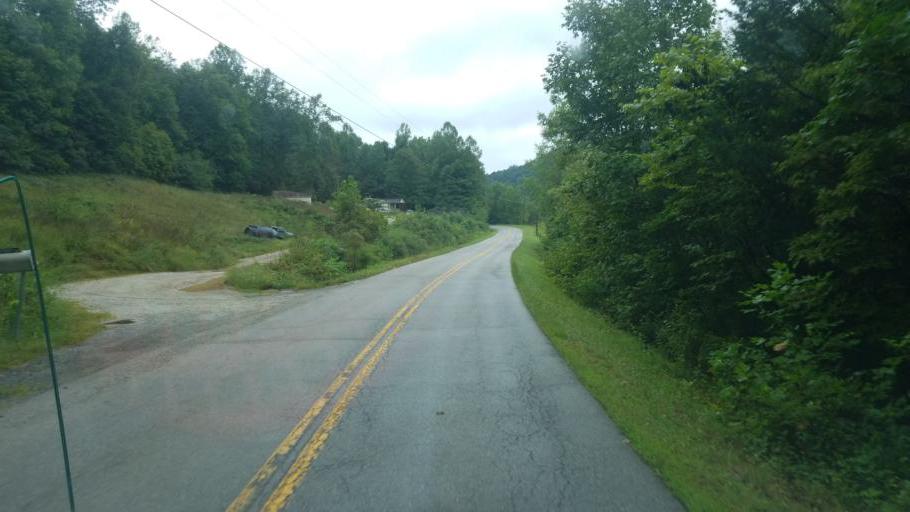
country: US
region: Kentucky
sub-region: Fleming County
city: Flemingsburg
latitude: 38.3795
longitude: -83.5412
